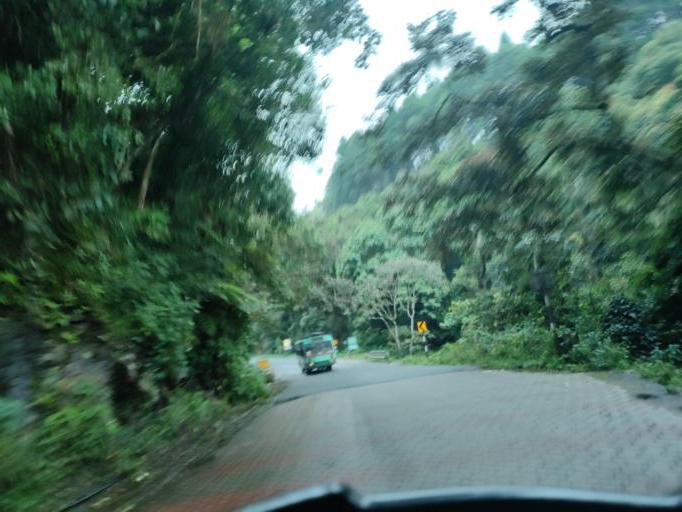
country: IN
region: Tamil Nadu
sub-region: Dindigul
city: Kodaikanal
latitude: 10.2457
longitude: 77.5169
